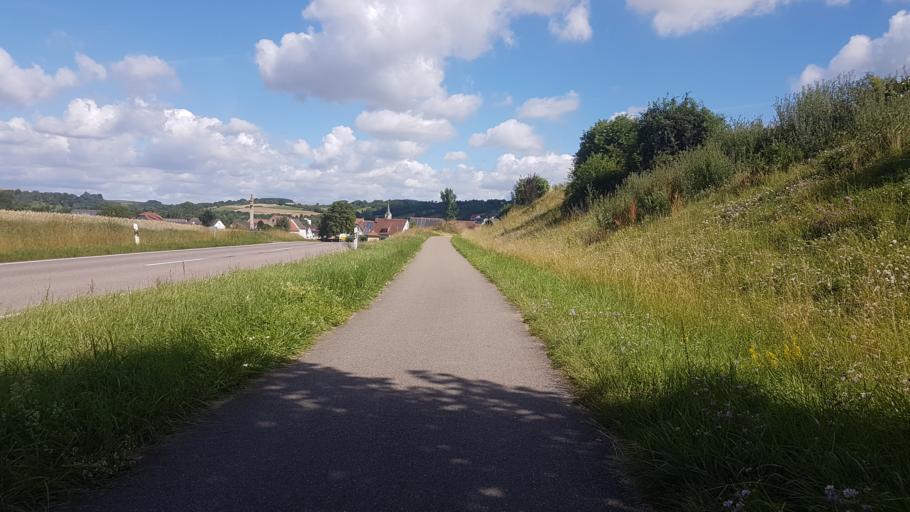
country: DE
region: Bavaria
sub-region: Regierungsbezirk Unterfranken
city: Bieberehren
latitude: 49.5114
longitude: 10.0107
